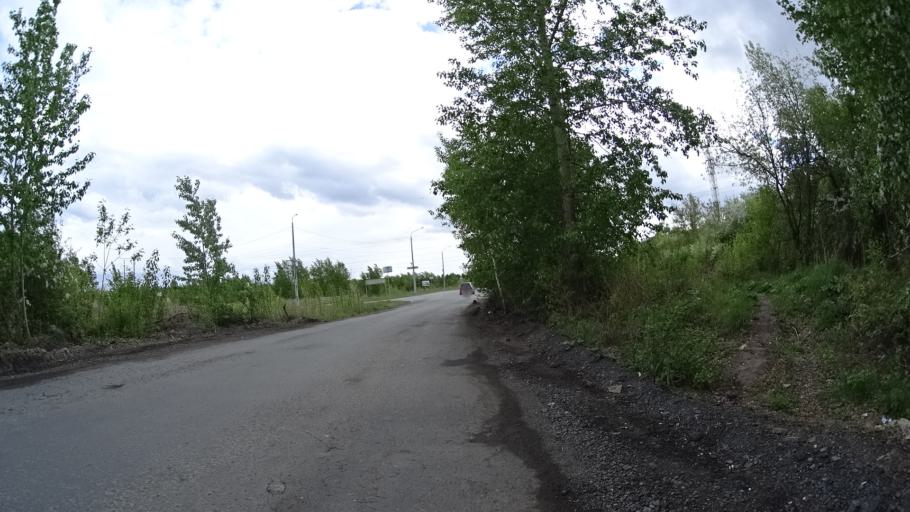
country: RU
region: Chelyabinsk
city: Sargazy
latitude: 55.1593
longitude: 61.2857
